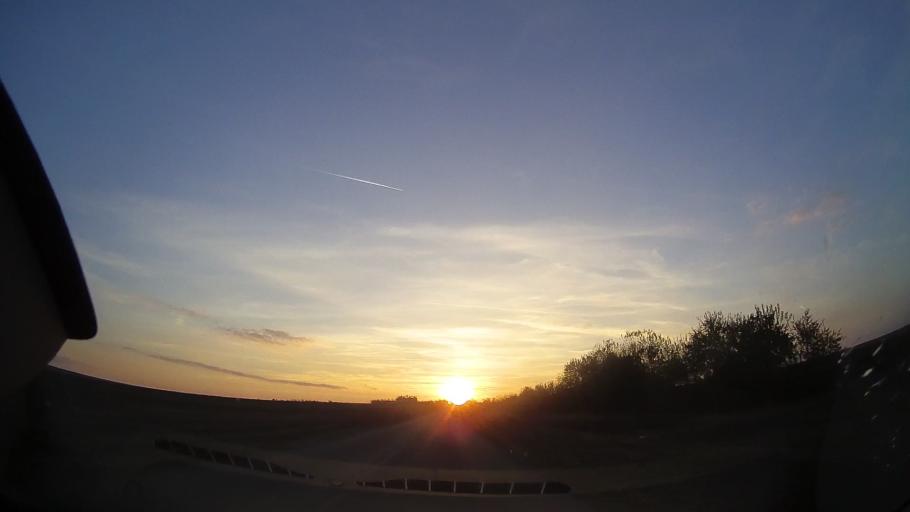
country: RO
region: Constanta
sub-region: Comuna Mereni
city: Mereni
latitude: 44.0250
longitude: 28.3623
